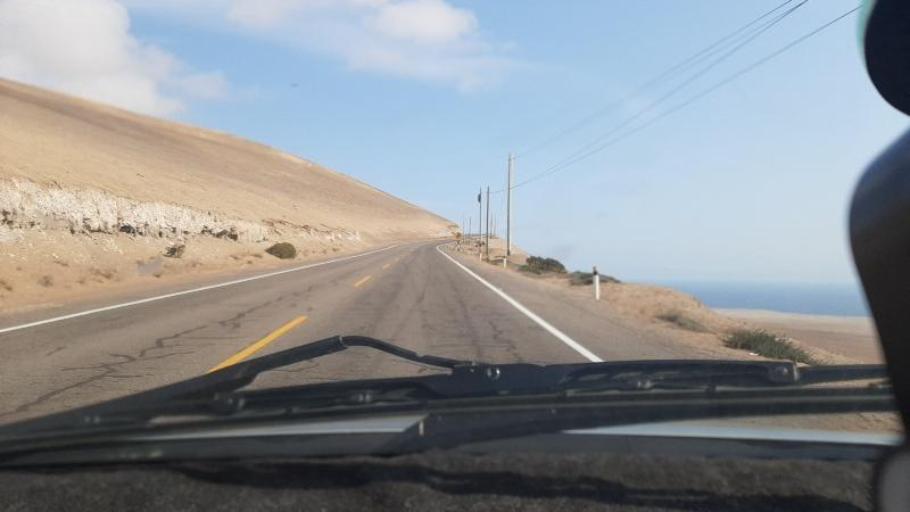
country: PE
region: Moquegua
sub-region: Provincia de Ilo
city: Ilo
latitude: -17.6803
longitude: -71.2918
